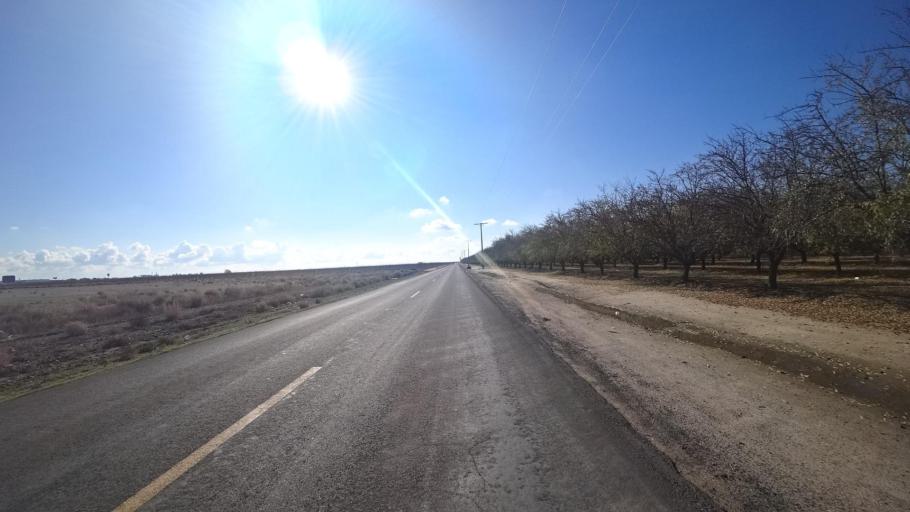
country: US
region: California
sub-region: Kern County
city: Delano
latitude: 35.7388
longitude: -119.2584
